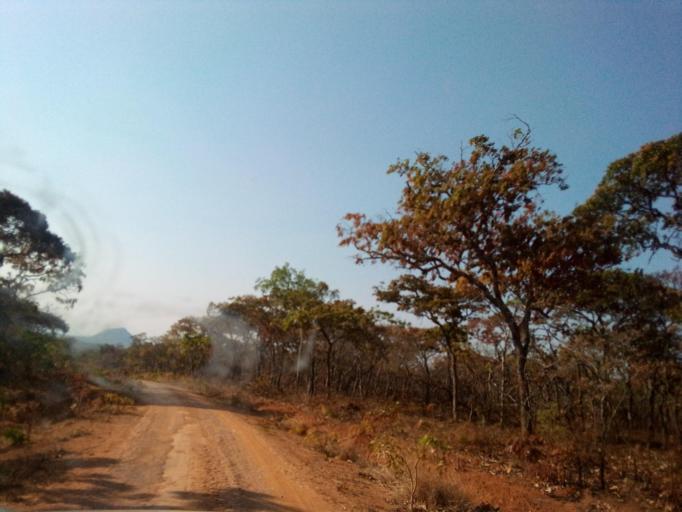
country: ZM
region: Northern
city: Mpika
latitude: -12.2171
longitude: 31.4399
